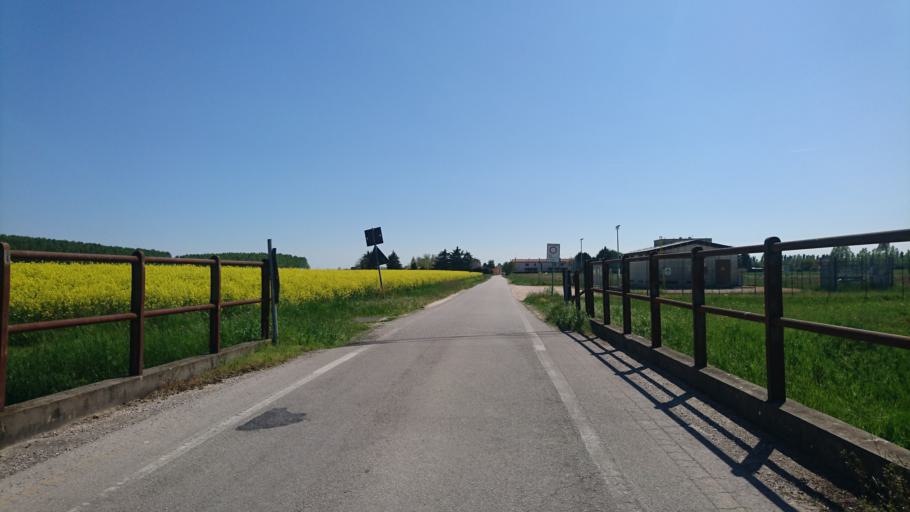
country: IT
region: Veneto
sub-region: Provincia di Treviso
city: Conscio
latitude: 45.5958
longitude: 12.2777
